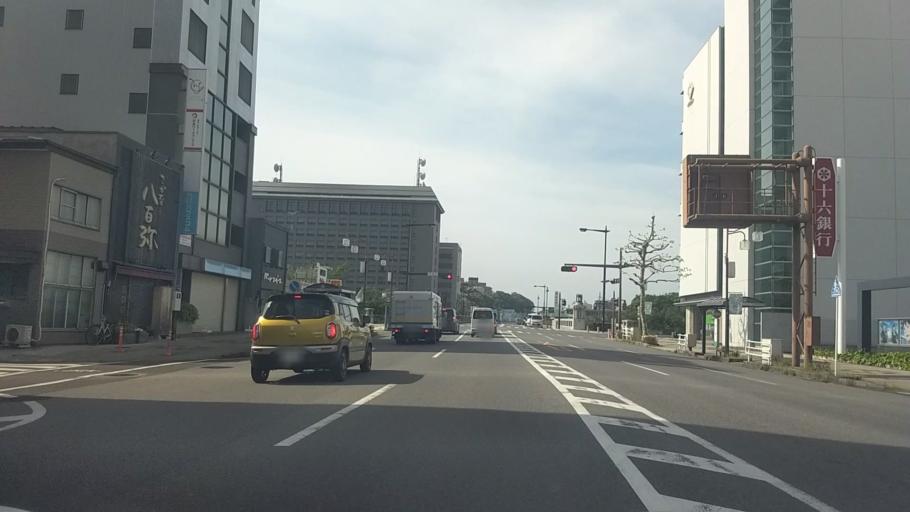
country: JP
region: Aichi
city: Okazaki
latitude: 34.9567
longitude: 137.1640
